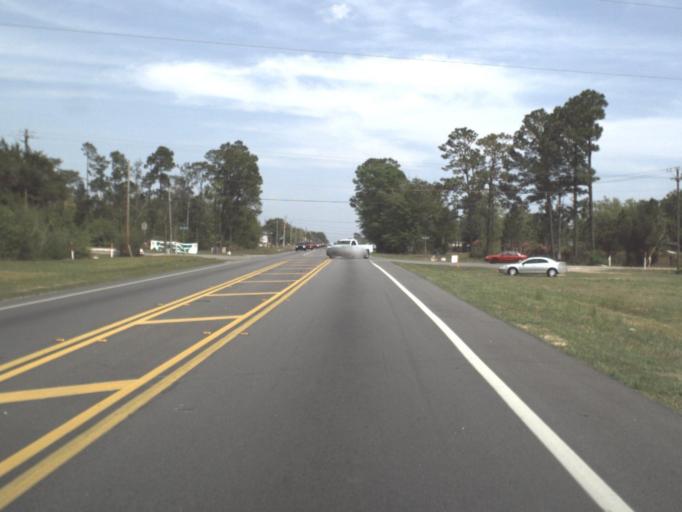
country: US
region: Florida
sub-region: Escambia County
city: Ensley
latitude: 30.5339
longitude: -87.2974
